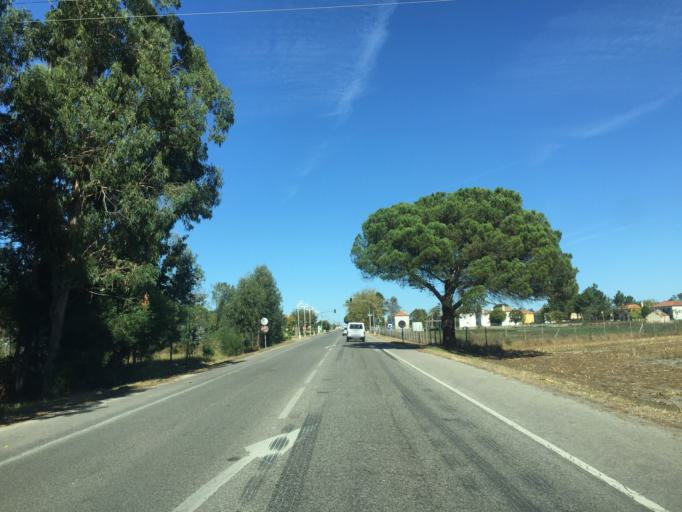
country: PT
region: Coimbra
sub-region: Montemor-O-Velho
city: Arazede
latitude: 40.2965
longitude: -8.7627
